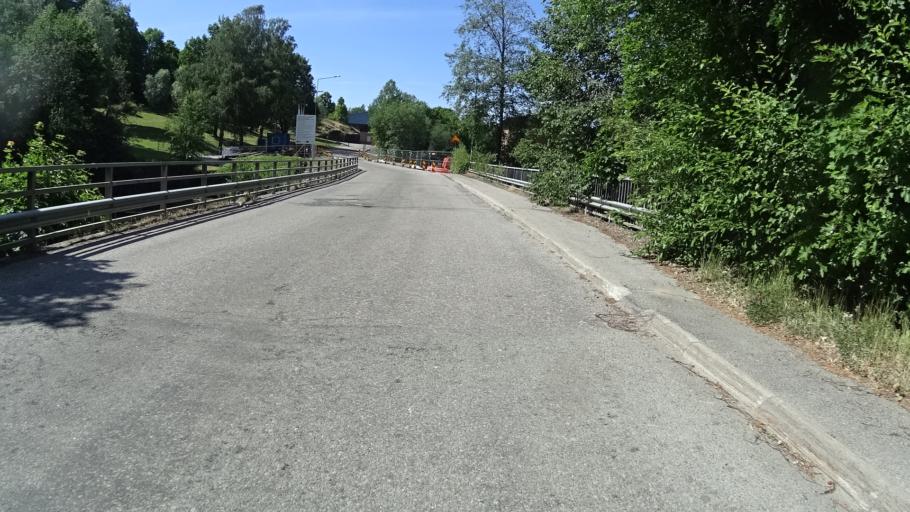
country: FI
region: Uusimaa
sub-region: Raaseporin
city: Pohja
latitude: 60.0955
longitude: 23.5914
